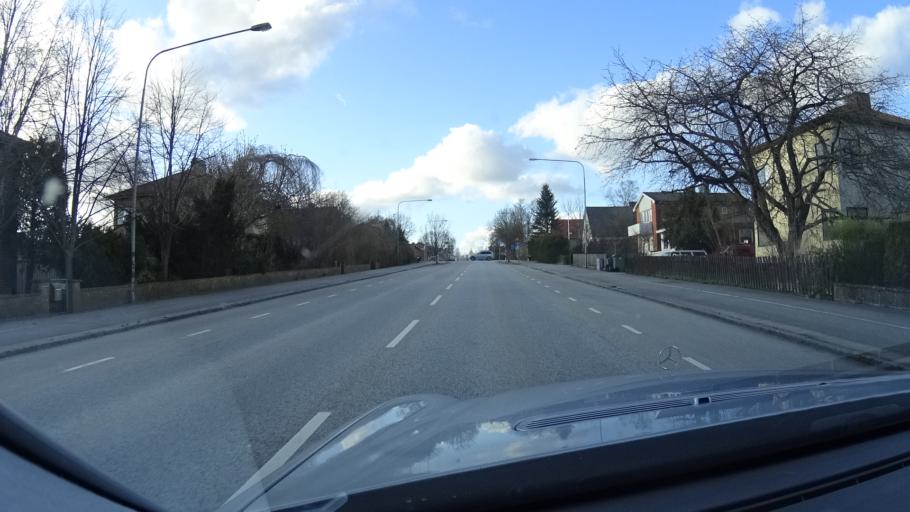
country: SE
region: Skane
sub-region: Hoors Kommun
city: Hoeoer
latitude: 55.9290
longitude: 13.5434
